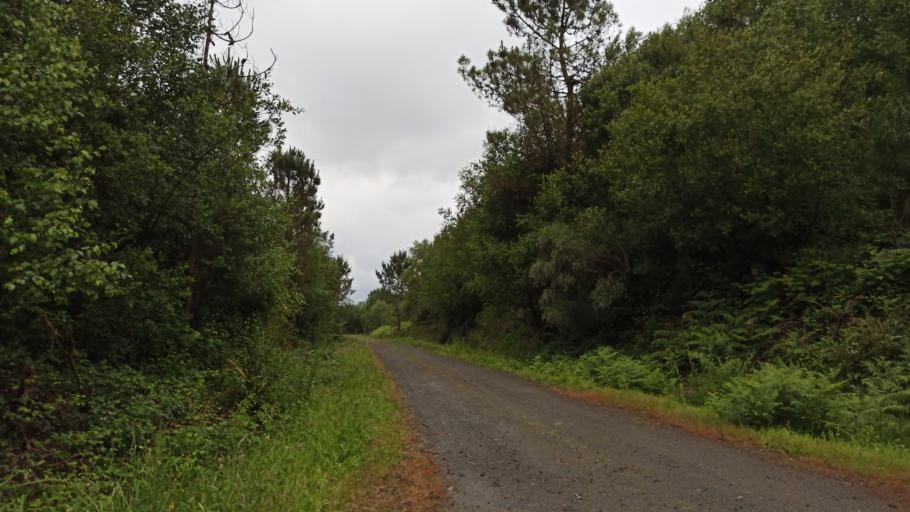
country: ES
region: Galicia
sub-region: Provincia da Coruna
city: Santiso
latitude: 42.7652
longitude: -8.0262
